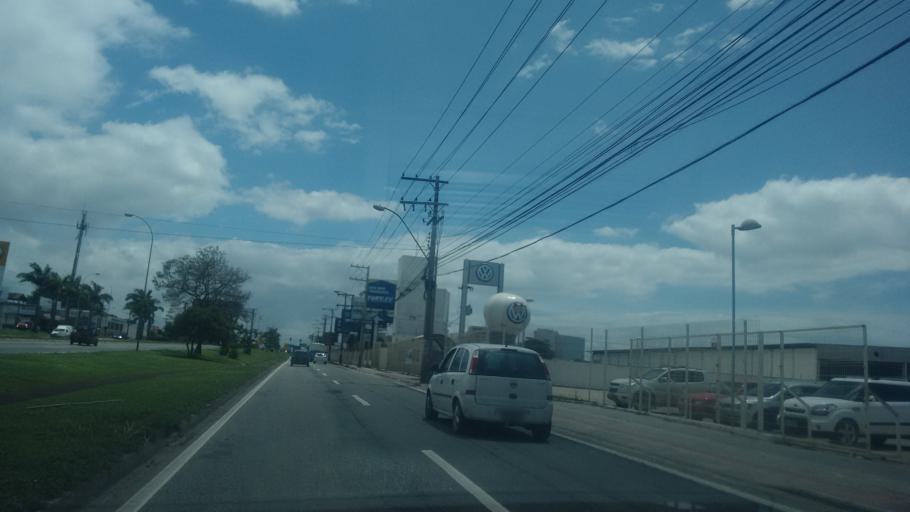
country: BR
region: Espirito Santo
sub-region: Serra
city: Serra
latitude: -20.1986
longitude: -40.2687
